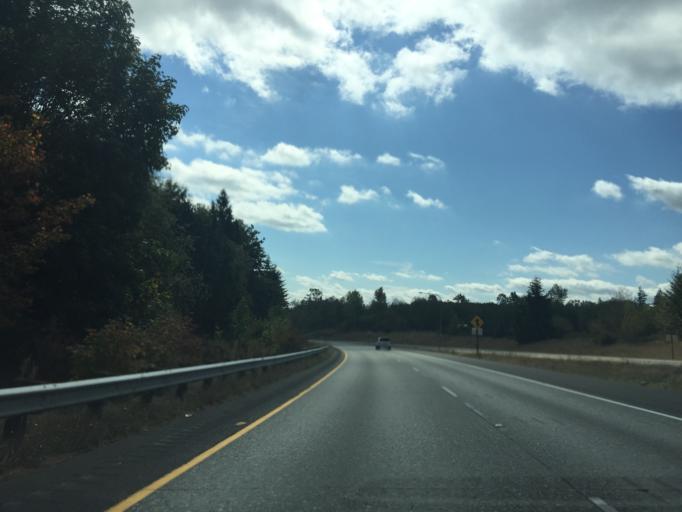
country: US
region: Washington
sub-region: Skagit County
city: Burlington
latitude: 48.5371
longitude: -122.3537
